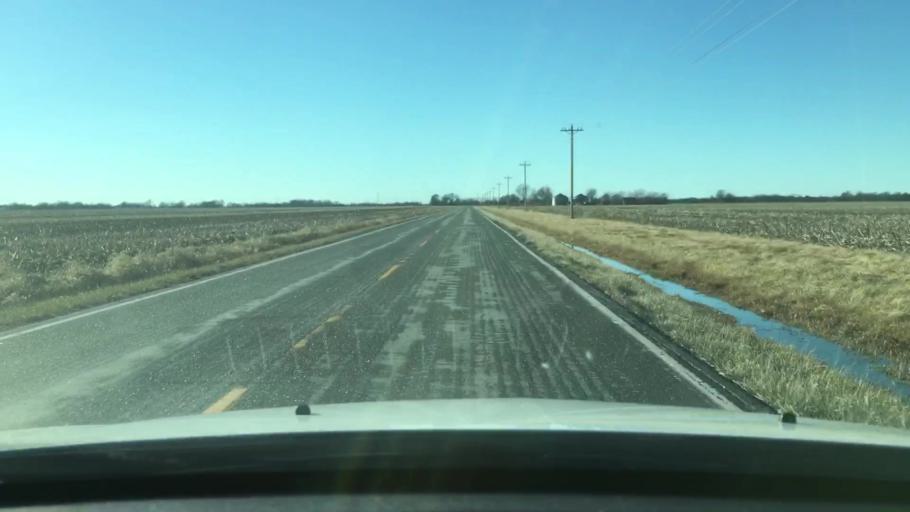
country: US
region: Missouri
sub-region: Audrain County
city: Mexico
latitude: 39.2817
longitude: -91.7303
